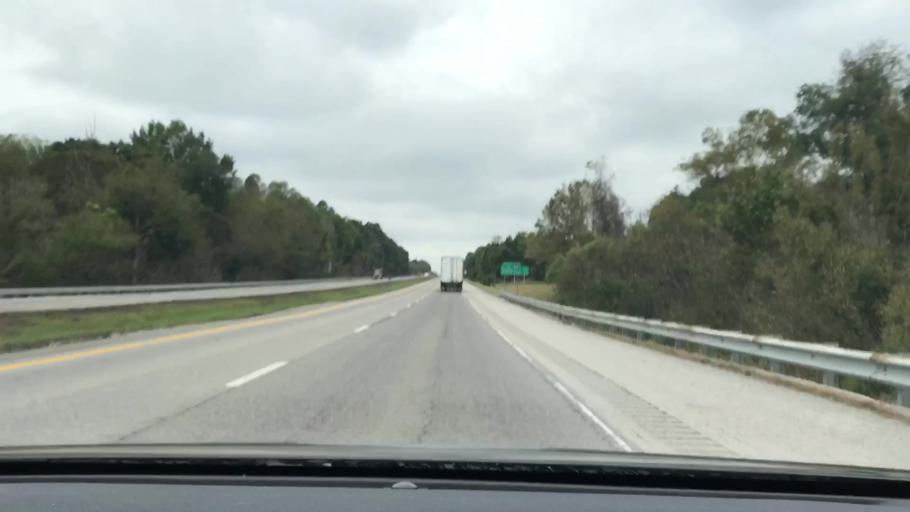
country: US
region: Kentucky
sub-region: Metcalfe County
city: Edmonton
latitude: 36.9963
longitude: -85.6664
